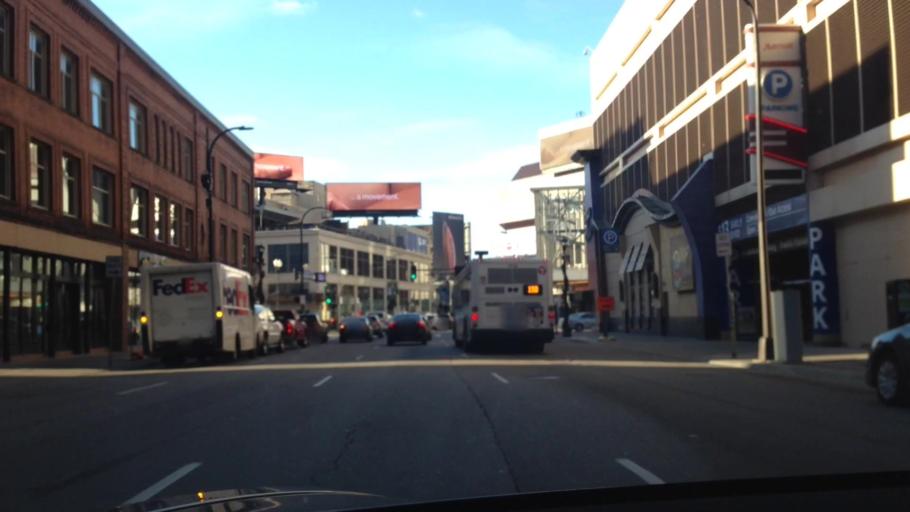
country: US
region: Minnesota
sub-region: Hennepin County
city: Minneapolis
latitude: 44.9776
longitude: -93.2739
